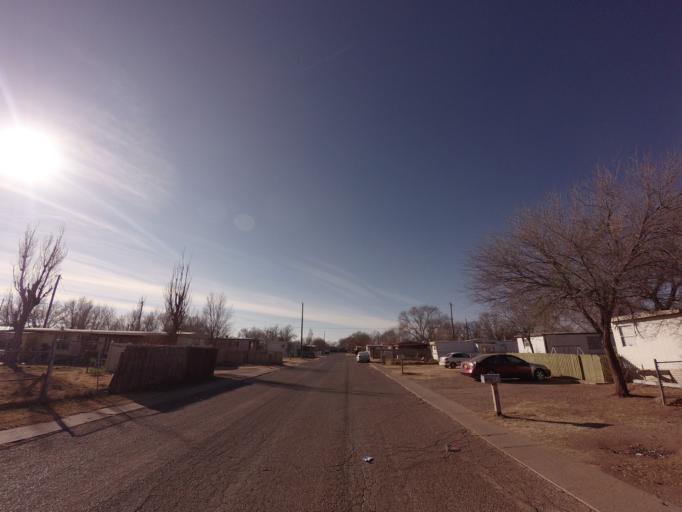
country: US
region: New Mexico
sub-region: Curry County
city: Clovis
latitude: 34.3885
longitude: -103.1999
